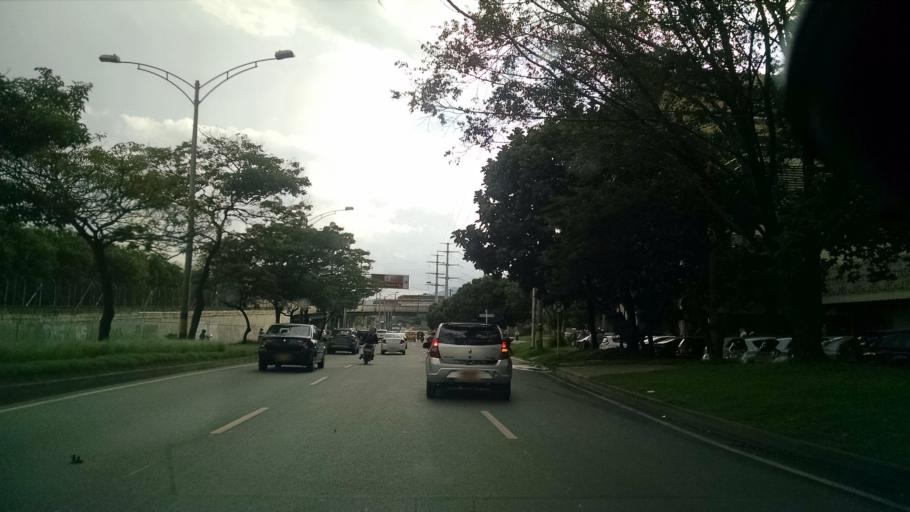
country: CO
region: Antioquia
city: Medellin
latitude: 6.2539
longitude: -75.5780
